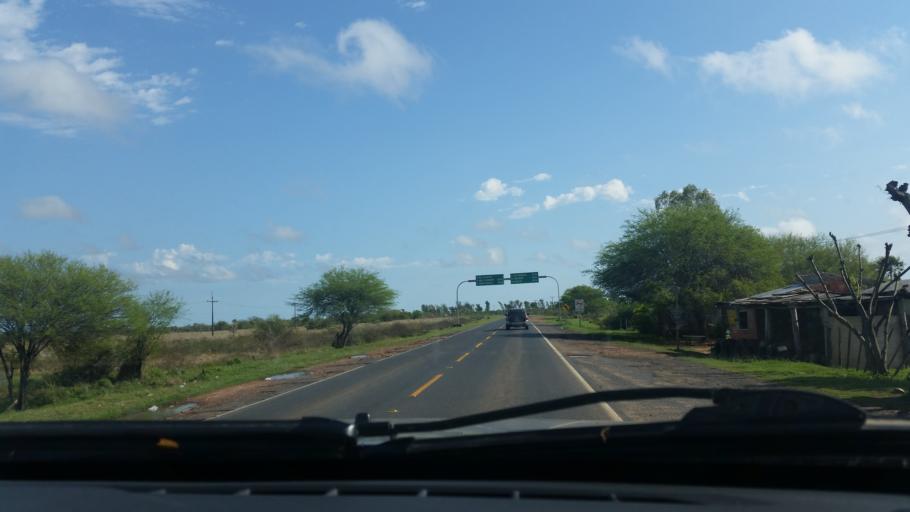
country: PY
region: Presidente Hayes
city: Benjamin Aceval
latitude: -24.9445
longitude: -57.5532
